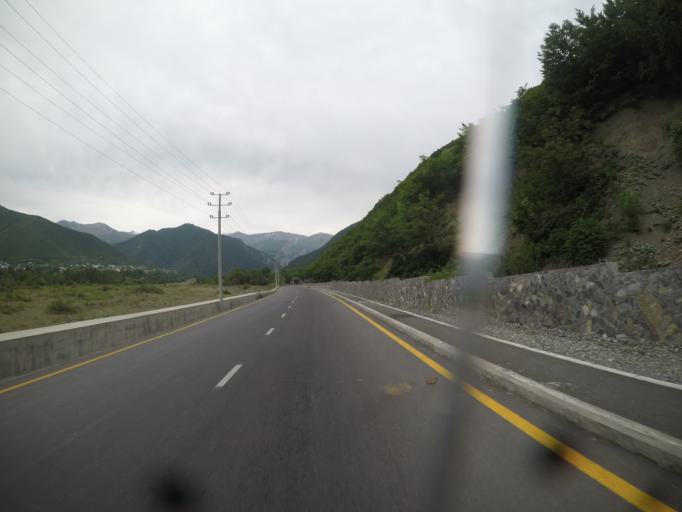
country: AZ
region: Shaki City
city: Sheki
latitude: 41.2426
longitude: 47.1949
